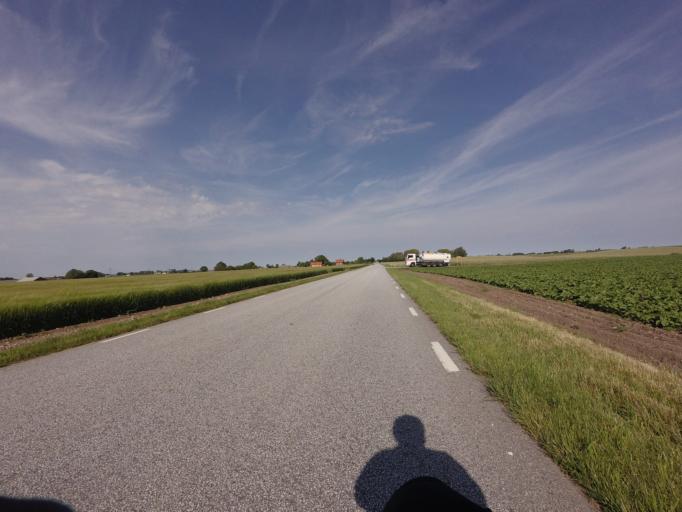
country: SE
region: Skane
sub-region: Malmo
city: Oxie
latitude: 55.4939
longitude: 13.0883
